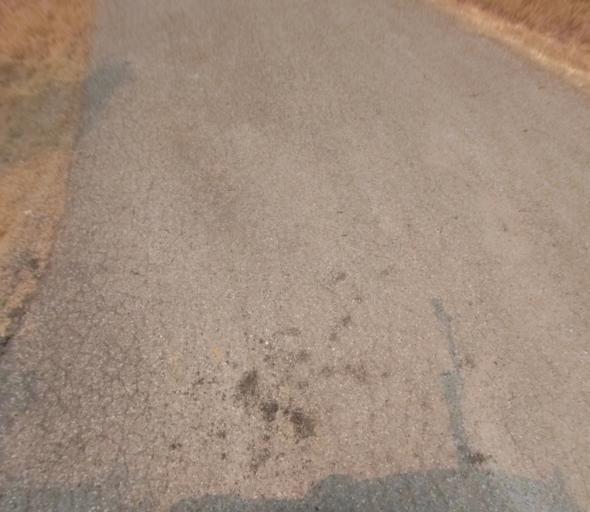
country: US
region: California
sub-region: Madera County
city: Oakhurst
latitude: 37.3417
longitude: -119.6168
